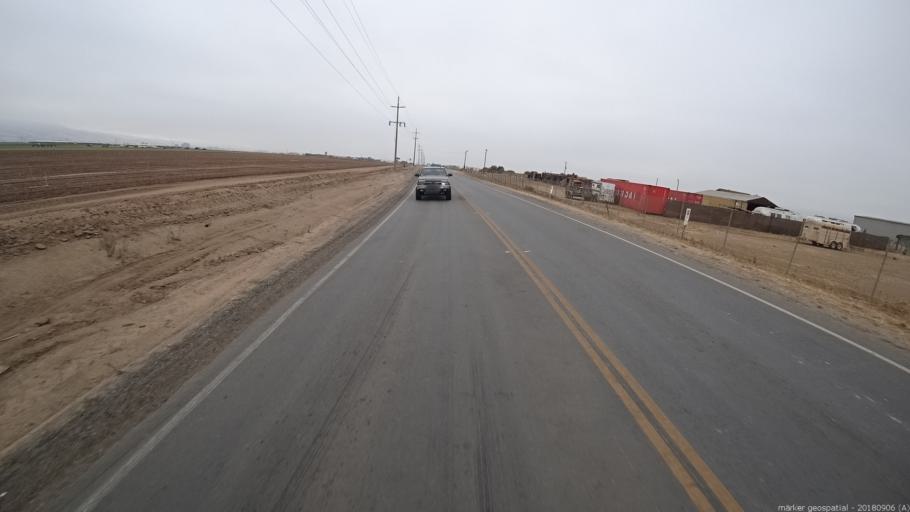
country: US
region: California
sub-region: Monterey County
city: Salinas
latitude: 36.6449
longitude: -121.5763
